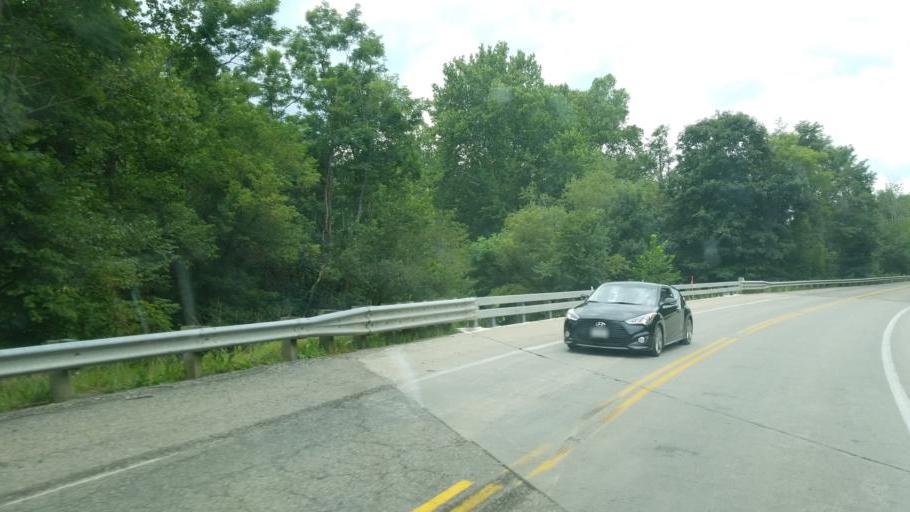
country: US
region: Ohio
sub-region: Columbiana County
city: Lisbon
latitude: 40.7654
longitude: -80.6950
